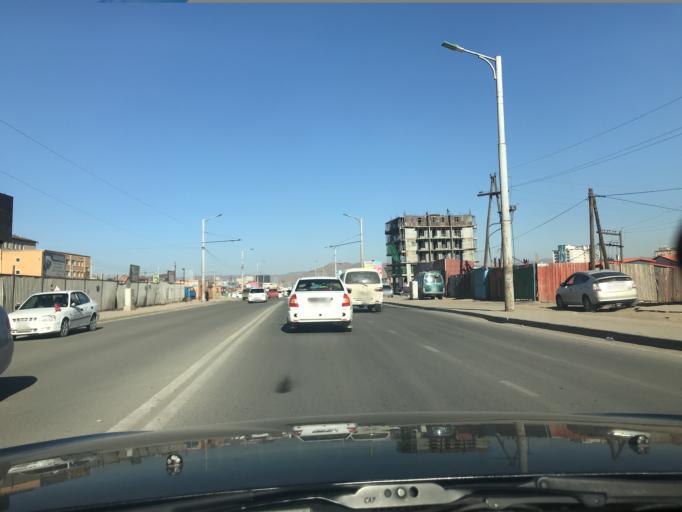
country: MN
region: Ulaanbaatar
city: Ulaanbaatar
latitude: 47.9342
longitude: 106.9069
